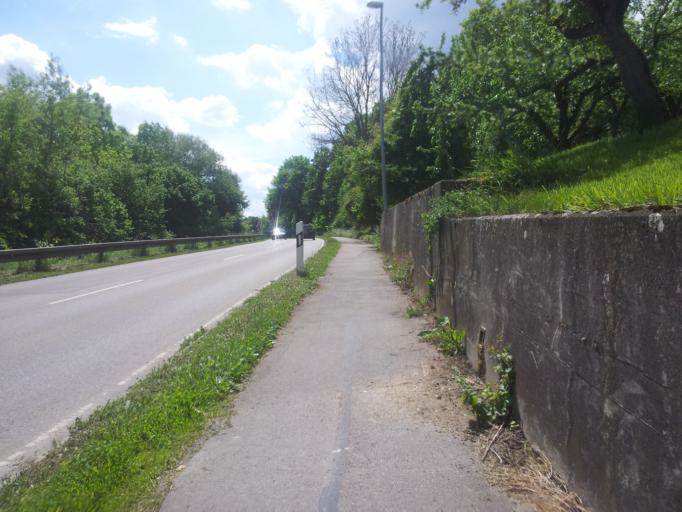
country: DE
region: Baden-Wuerttemberg
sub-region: Regierungsbezirk Stuttgart
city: Unterensingen
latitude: 48.6478
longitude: 9.3522
